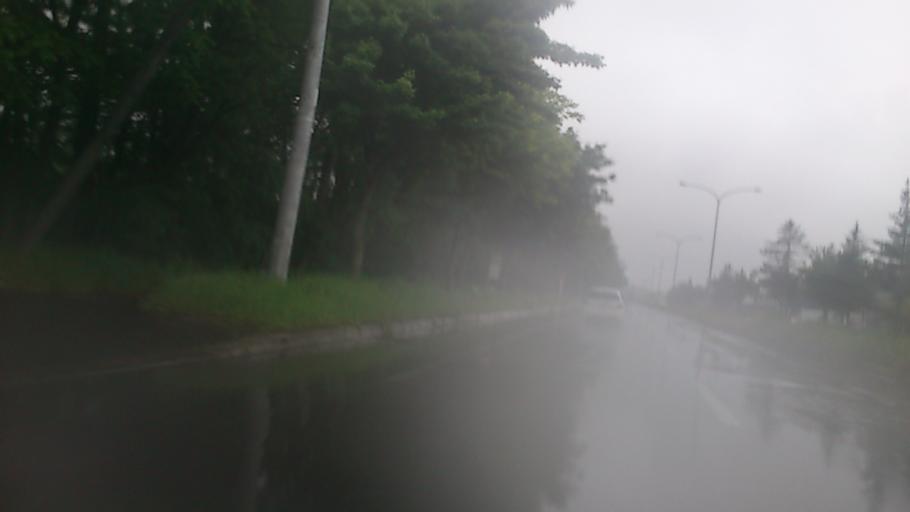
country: JP
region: Hokkaido
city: Obihiro
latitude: 42.9072
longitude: 143.1373
